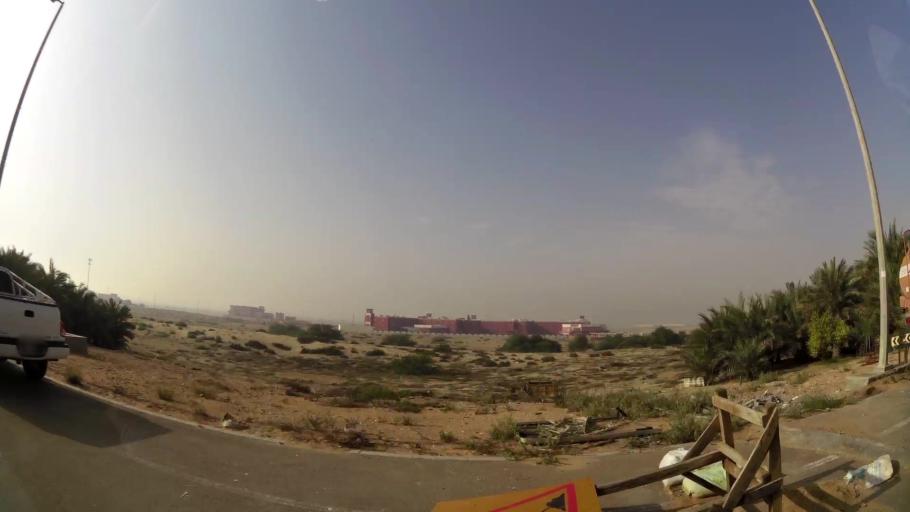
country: AE
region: Abu Dhabi
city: Abu Dhabi
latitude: 24.2676
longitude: 54.6609
